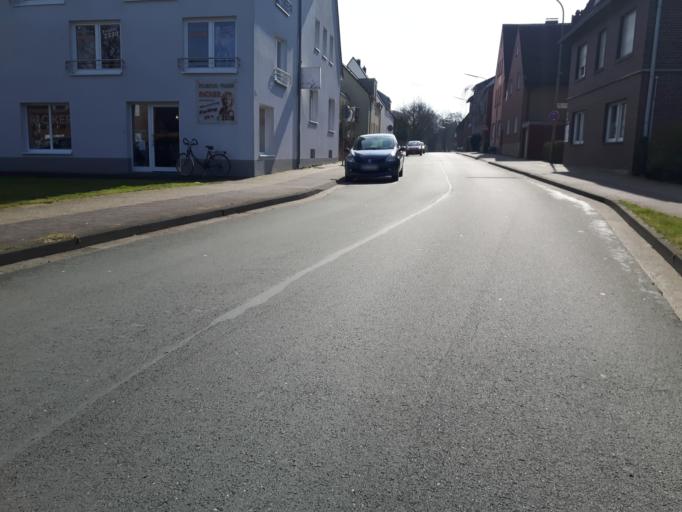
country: DE
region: North Rhine-Westphalia
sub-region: Regierungsbezirk Munster
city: Dulmen
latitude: 51.8303
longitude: 7.2862
